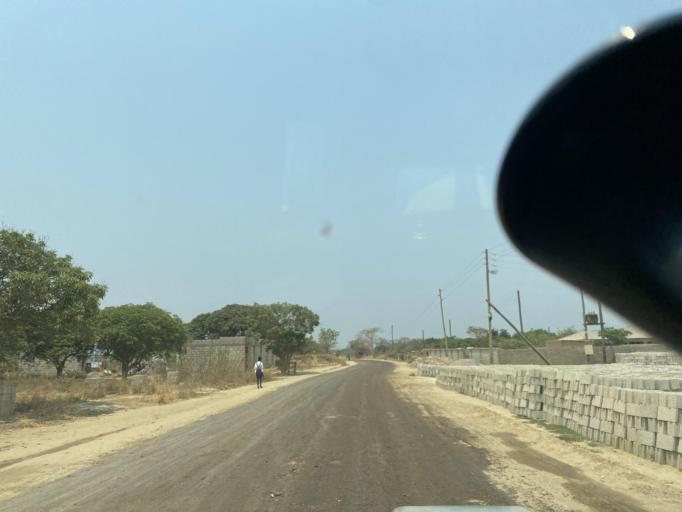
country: ZM
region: Lusaka
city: Lusaka
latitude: -15.5465
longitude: 28.3581
